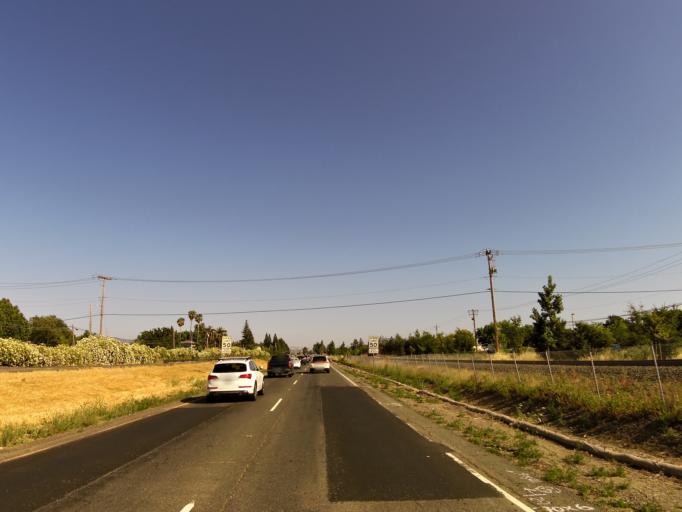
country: US
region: California
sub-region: Napa County
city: Napa
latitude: 38.3351
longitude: -122.3210
